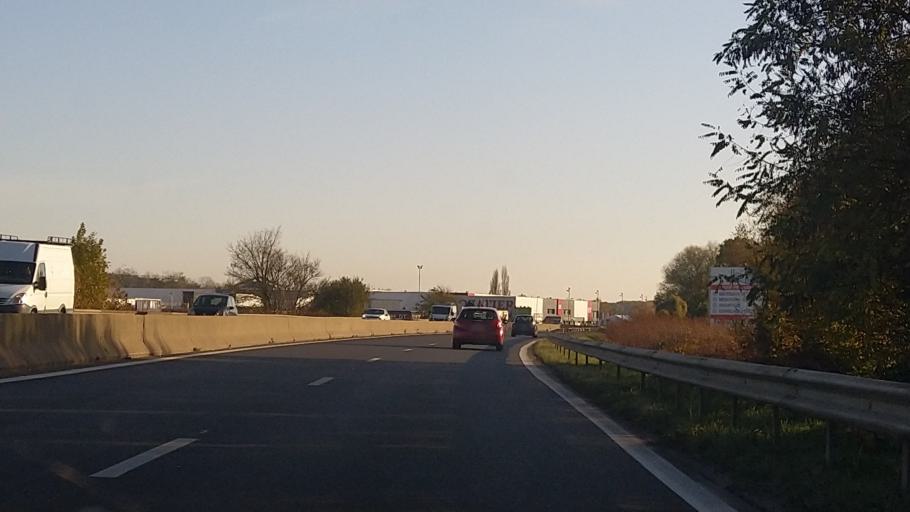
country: FR
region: Ile-de-France
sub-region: Departement du Val-d'Oise
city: Moisselles
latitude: 49.0402
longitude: 2.3431
